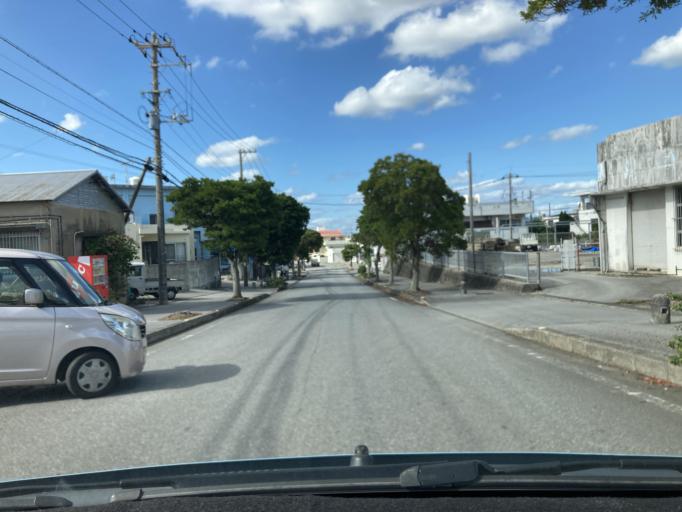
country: JP
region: Okinawa
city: Gushikawa
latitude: 26.3638
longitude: 127.8468
